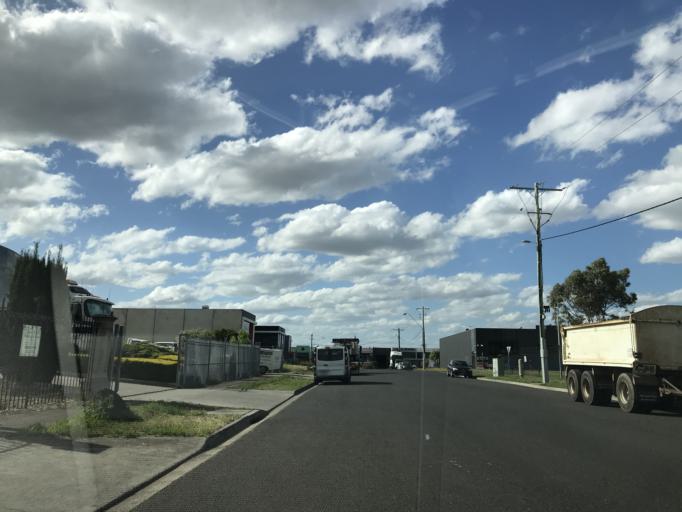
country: AU
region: Victoria
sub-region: Brimbank
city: Sunshine West
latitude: -37.8062
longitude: 144.8152
